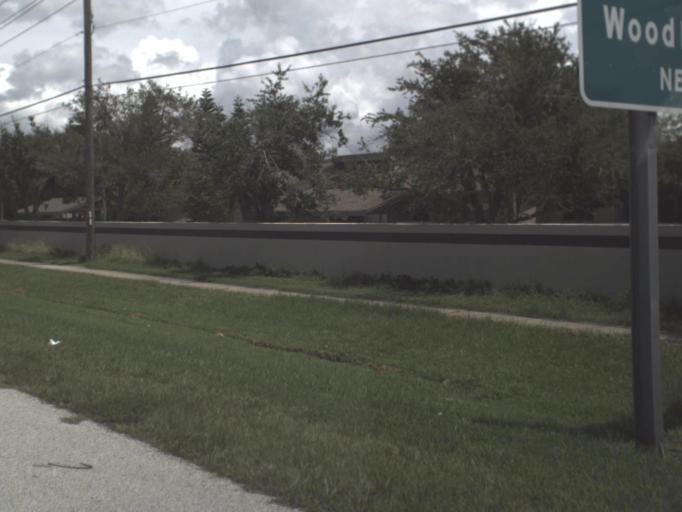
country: US
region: Florida
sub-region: Pinellas County
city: Saint George
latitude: 28.0727
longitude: -82.7041
